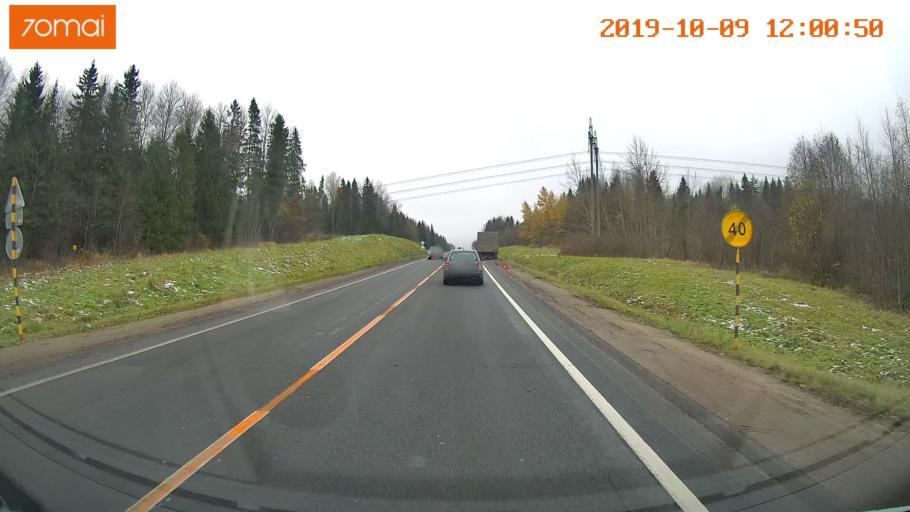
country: RU
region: Vologda
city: Gryazovets
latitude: 58.6940
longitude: 40.3009
